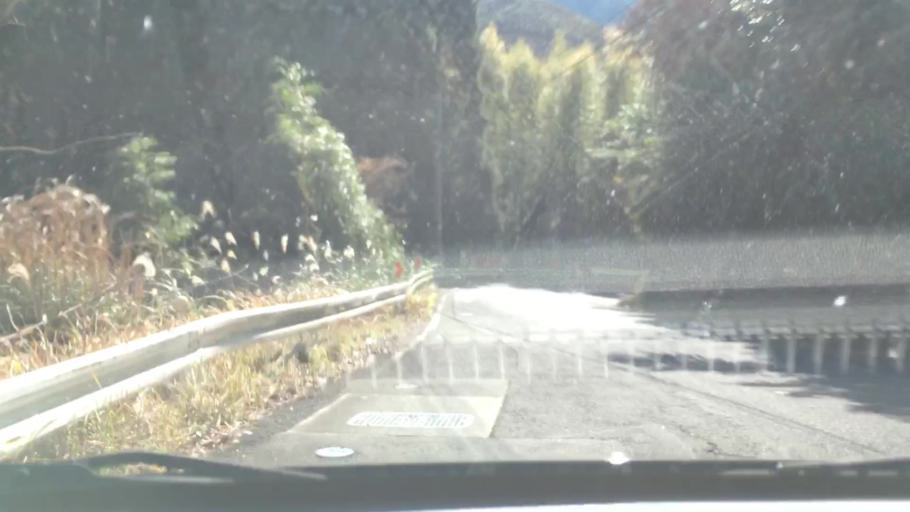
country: JP
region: Kagoshima
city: Ijuin
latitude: 31.7122
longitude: 130.4230
